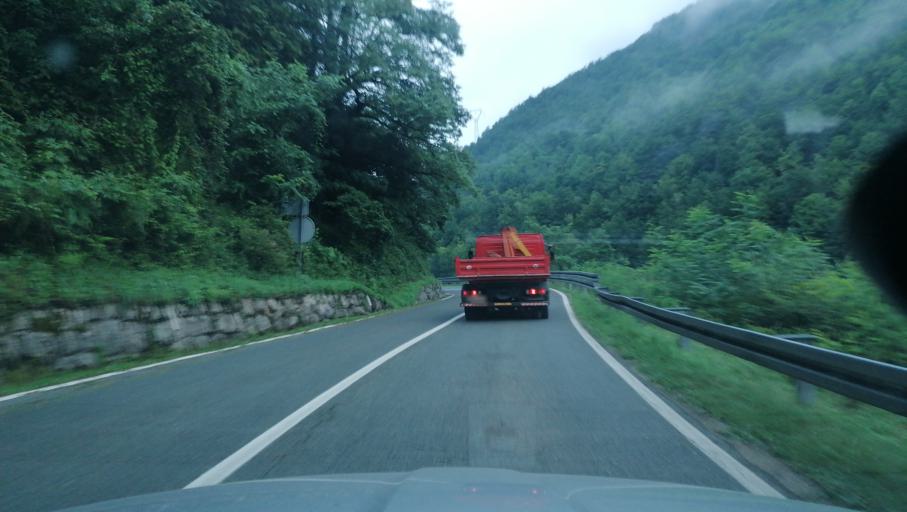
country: BA
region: Federation of Bosnia and Herzegovina
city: Jablanica
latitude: 43.7317
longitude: 17.6813
